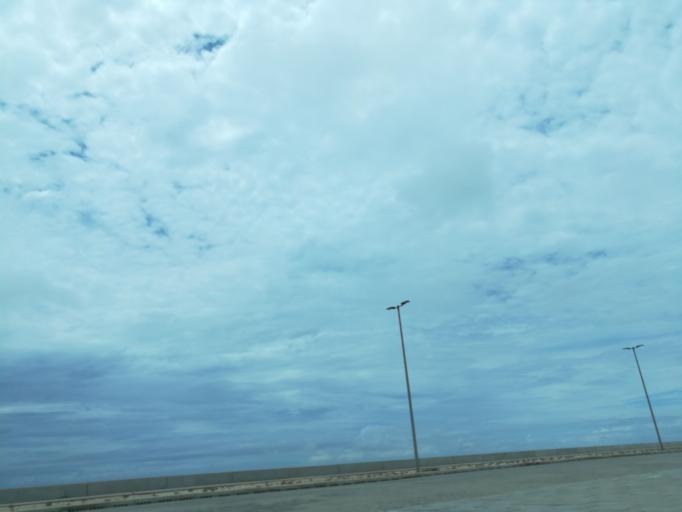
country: NG
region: Lagos
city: Ikoyi
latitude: 6.4052
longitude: 3.4174
